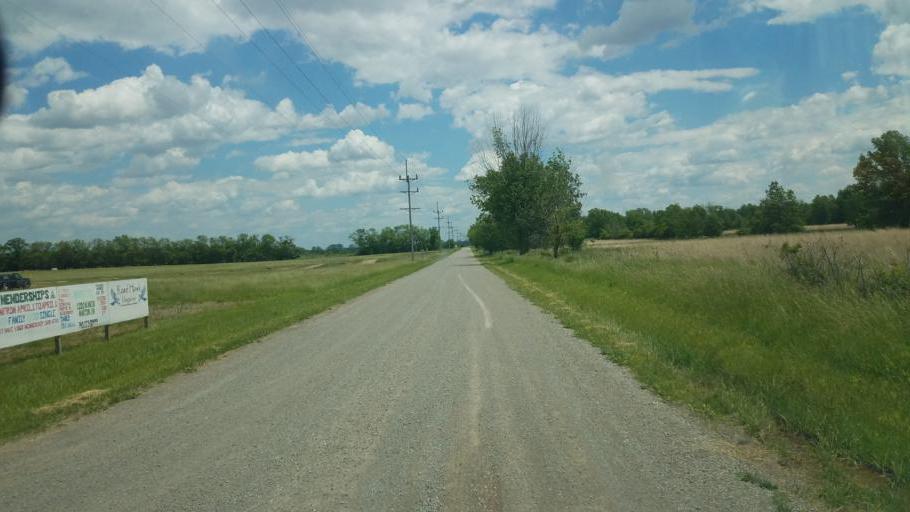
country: US
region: Ohio
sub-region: Wyandot County
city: Upper Sandusky
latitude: 40.7241
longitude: -83.2666
